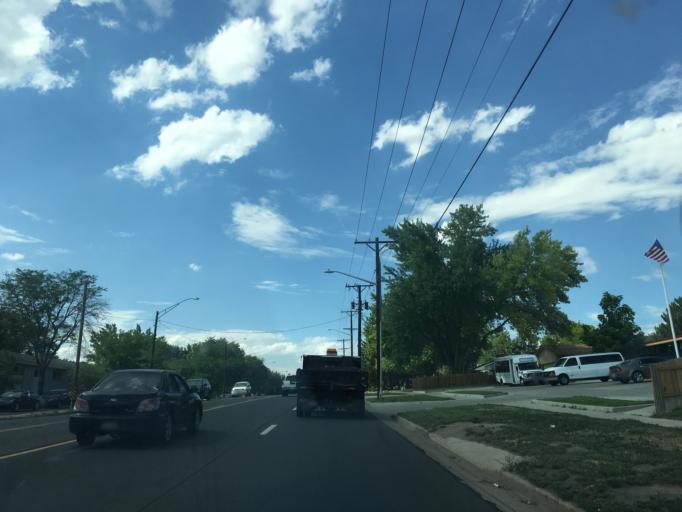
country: US
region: Colorado
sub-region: Arapahoe County
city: Sheridan
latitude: 39.6693
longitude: -105.0532
